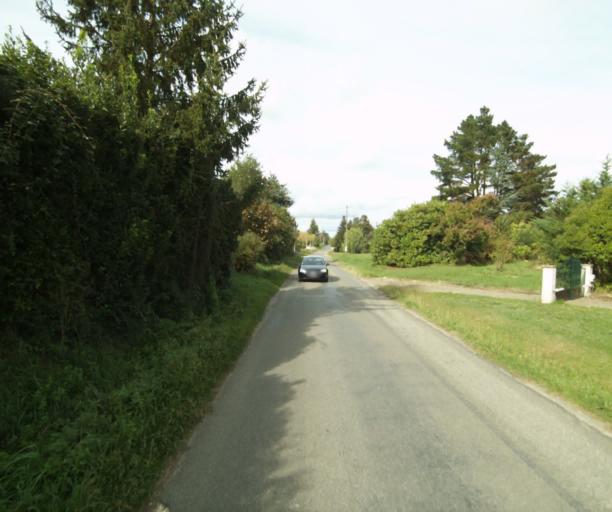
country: FR
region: Midi-Pyrenees
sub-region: Departement du Gers
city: Eauze
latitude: 43.8477
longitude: 0.1056
